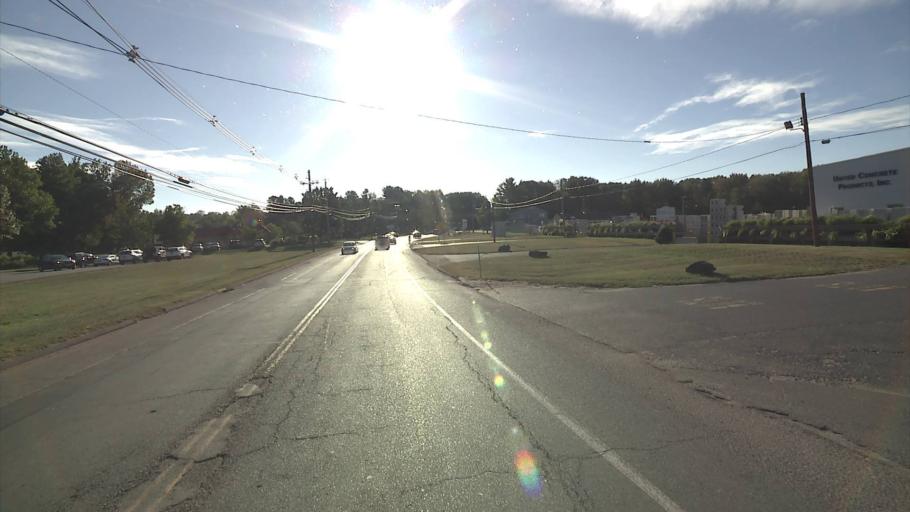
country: US
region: Connecticut
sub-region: New Haven County
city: Wallingford
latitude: 41.4905
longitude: -72.8148
